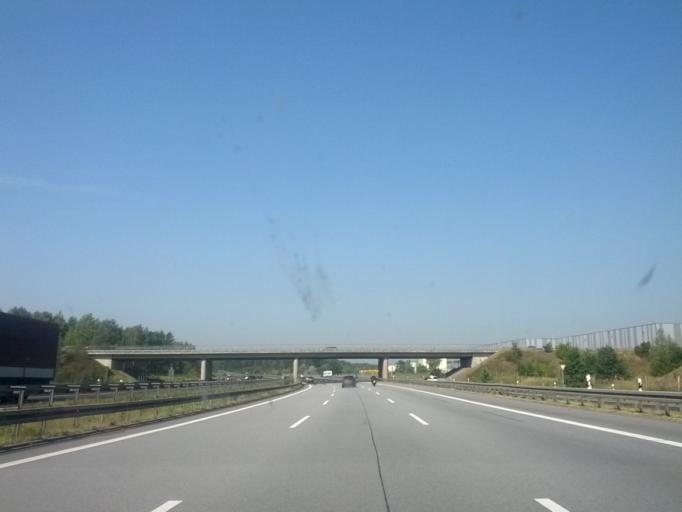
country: DE
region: Brandenburg
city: Ludwigsfelde
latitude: 52.3085
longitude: 13.2847
